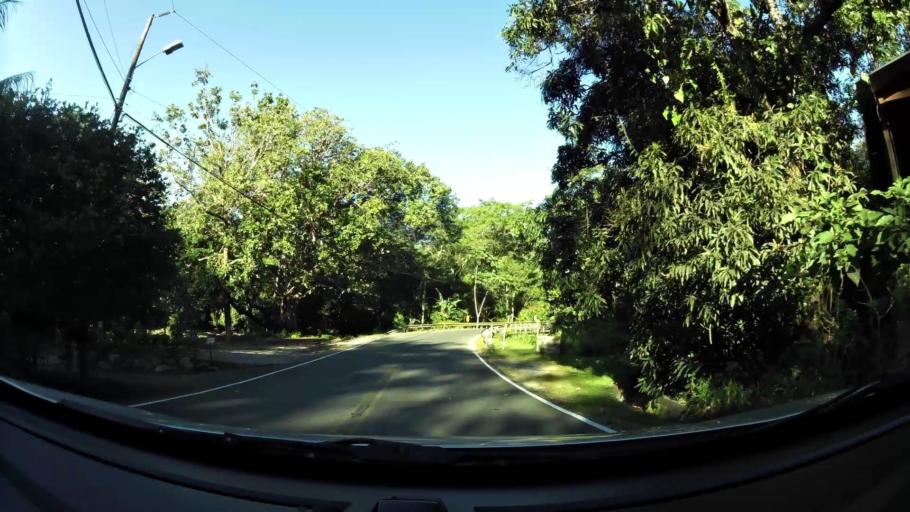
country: CR
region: Guanacaste
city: Juntas
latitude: 10.1987
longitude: -84.8438
